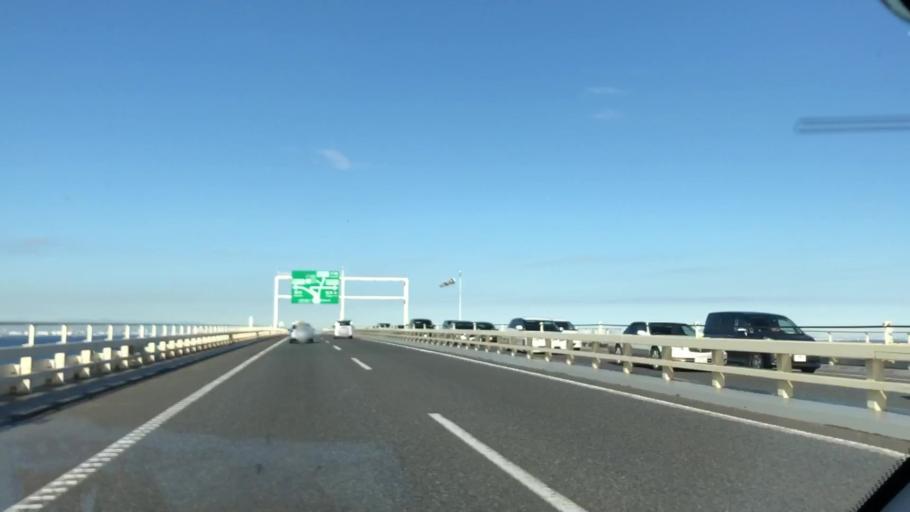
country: JP
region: Chiba
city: Kisarazu
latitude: 35.4546
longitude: 139.8886
